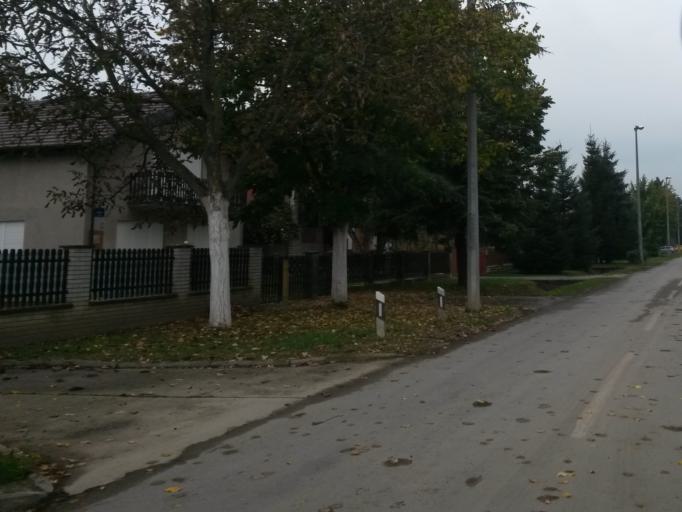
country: HR
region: Osjecko-Baranjska
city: Brijest
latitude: 45.5170
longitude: 18.6288
